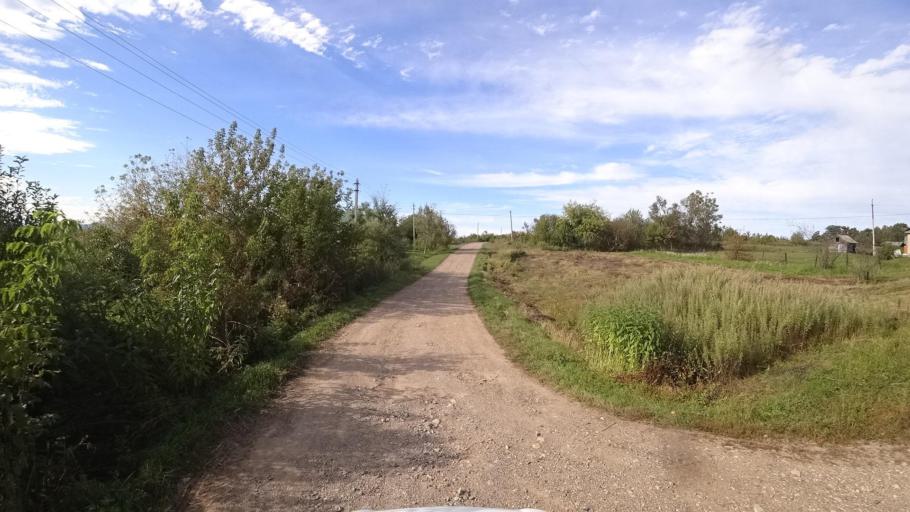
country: RU
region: Primorskiy
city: Dostoyevka
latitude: 44.2946
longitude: 133.4485
